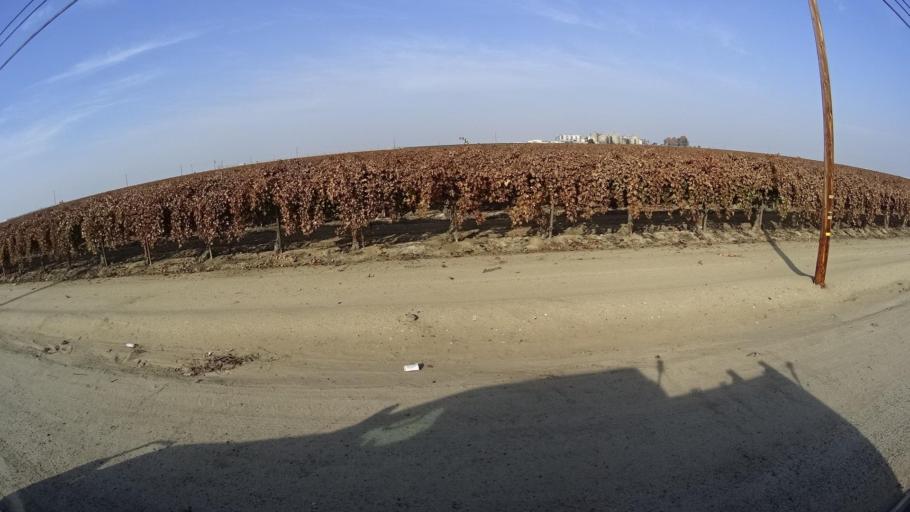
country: US
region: California
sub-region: Kern County
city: Delano
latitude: 35.7760
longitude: -119.1935
